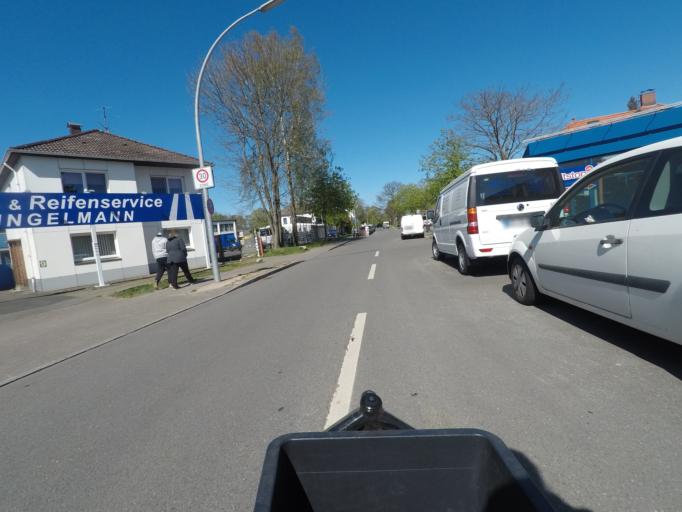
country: DE
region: Hamburg
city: Farmsen-Berne
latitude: 53.5932
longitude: 10.1378
